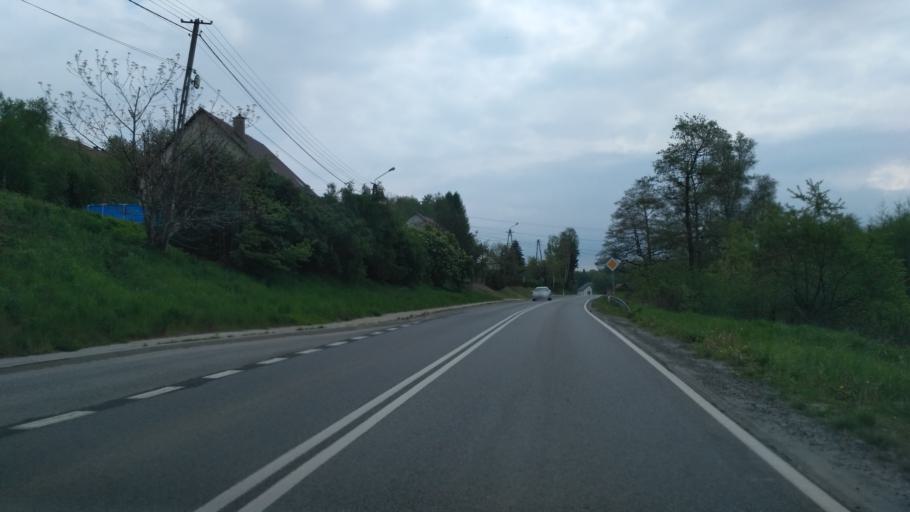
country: PL
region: Lesser Poland Voivodeship
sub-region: Powiat tarnowski
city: Tarnowiec
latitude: 49.9574
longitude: 20.9982
